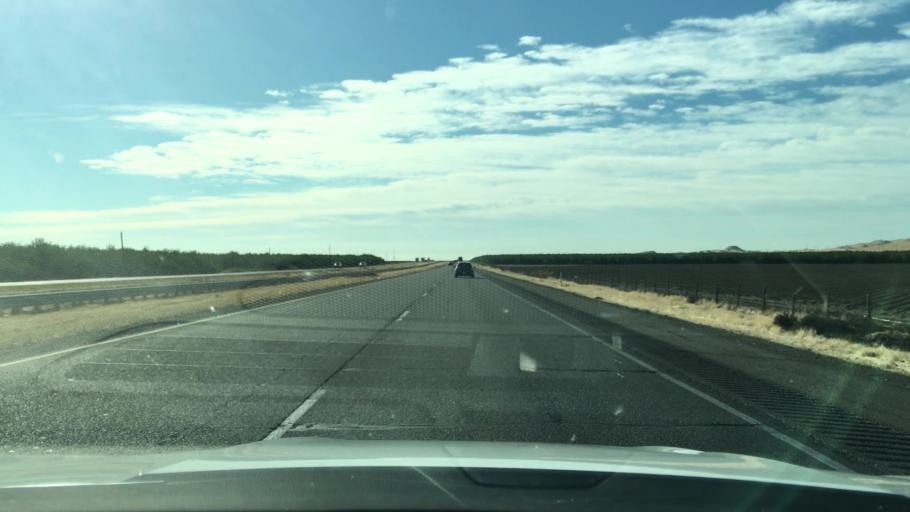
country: US
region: California
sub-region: Fresno County
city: Coalinga
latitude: 36.3896
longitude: -120.3531
